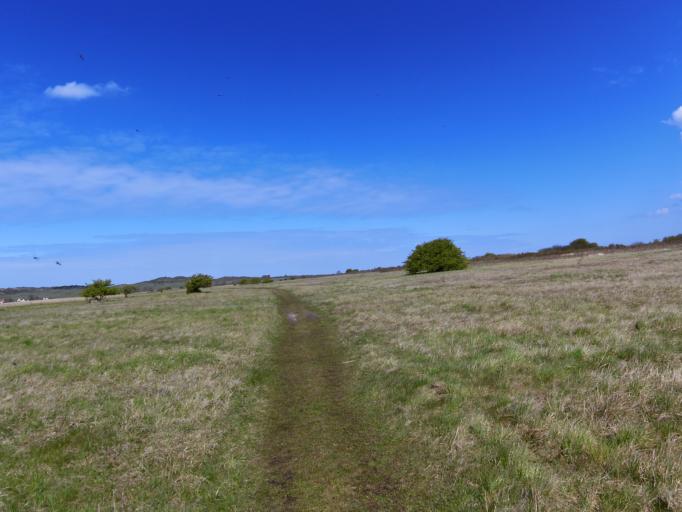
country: DE
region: Mecklenburg-Vorpommern
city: Hiddensee
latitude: 54.5831
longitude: 13.1434
